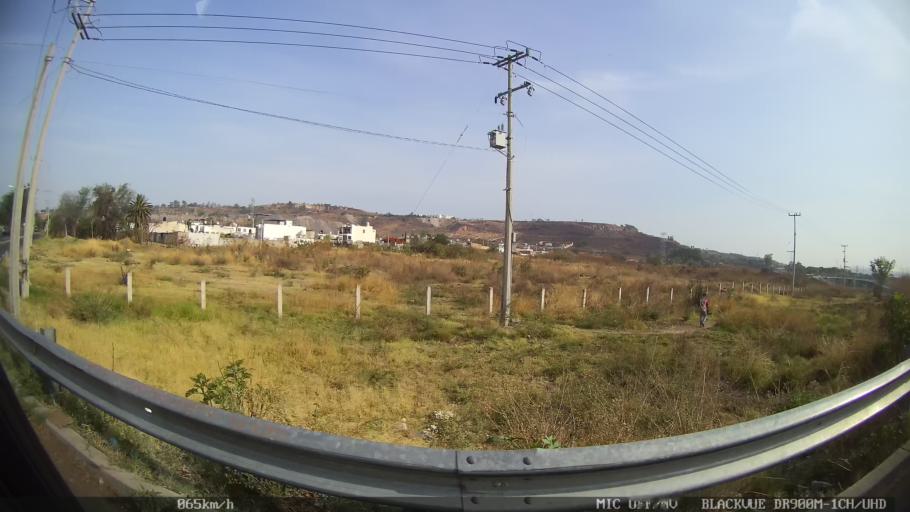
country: MX
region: Jalisco
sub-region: Tonala
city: Paseo de las Canadas
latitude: 20.6240
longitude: -103.2114
